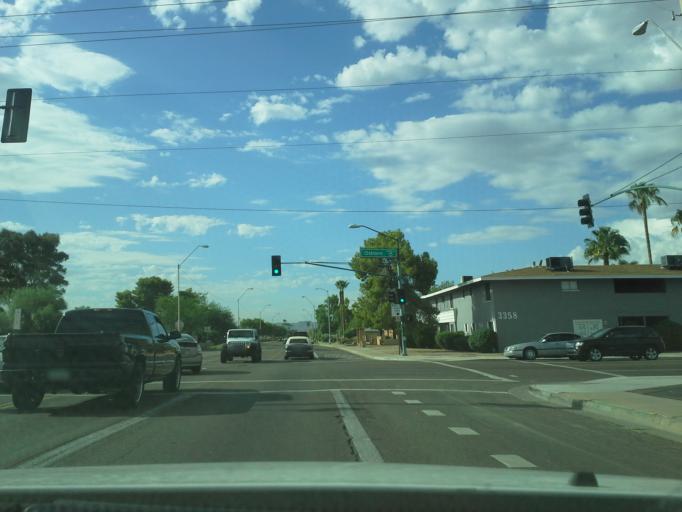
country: US
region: Arizona
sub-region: Maricopa County
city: Phoenix
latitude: 33.4881
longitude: -112.0914
